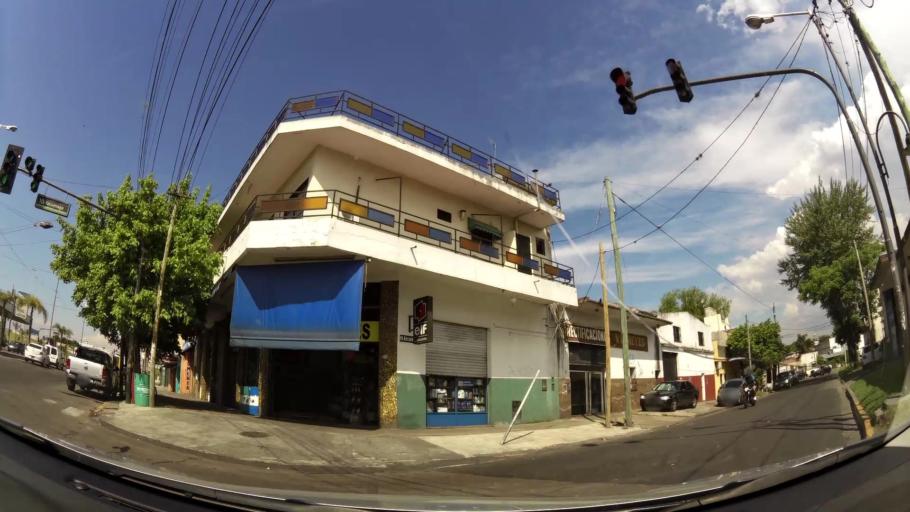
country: AR
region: Buenos Aires
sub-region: Partido de Tigre
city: Tigre
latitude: -34.4614
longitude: -58.5737
